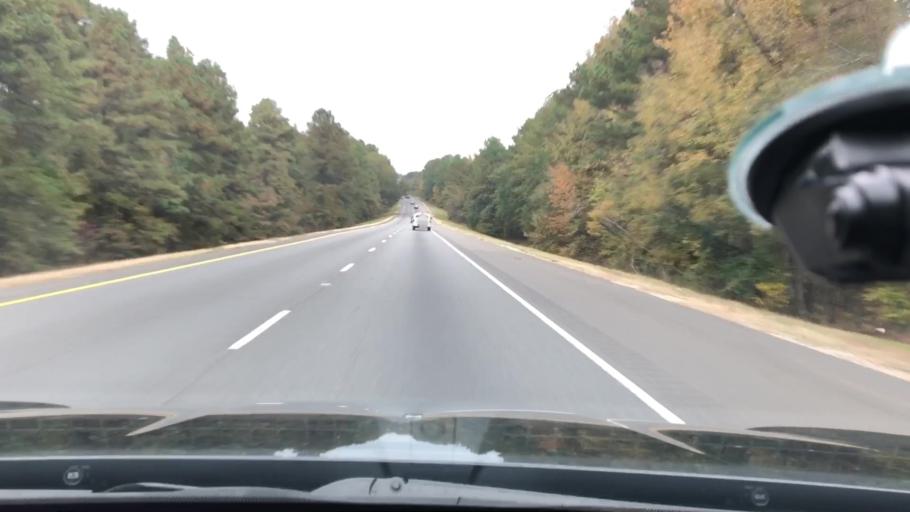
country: US
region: Arkansas
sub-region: Hot Spring County
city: Malvern
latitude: 34.3048
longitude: -92.9424
